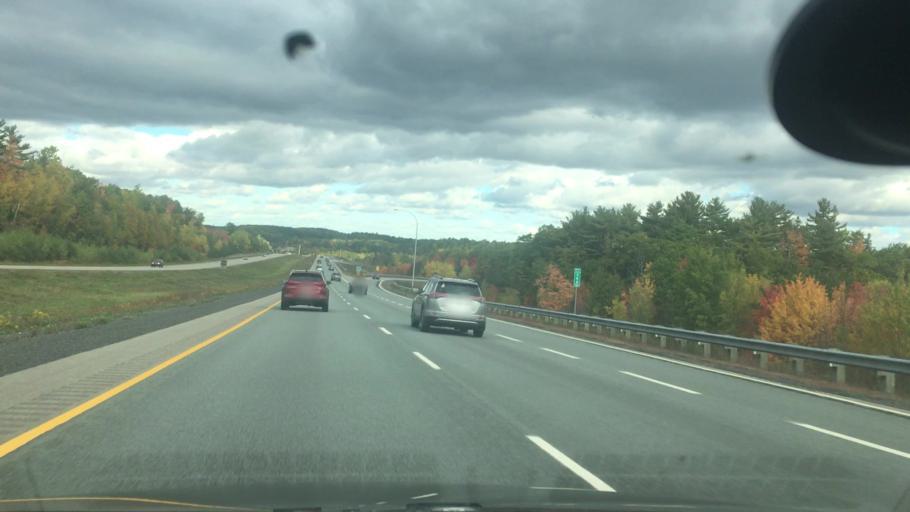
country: CA
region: Nova Scotia
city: Windsor
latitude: 44.9551
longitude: -64.0108
